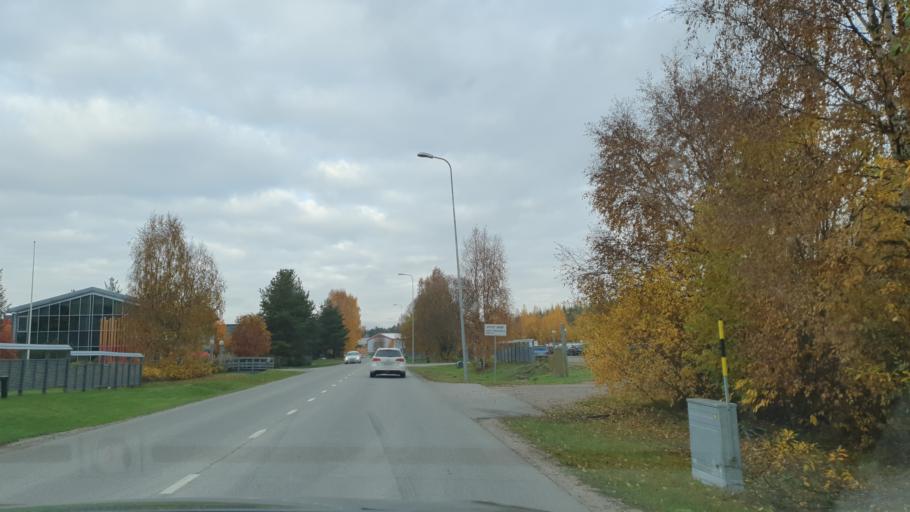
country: FI
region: Lapland
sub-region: Rovaniemi
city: Rovaniemi
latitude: 66.4938
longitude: 25.6761
